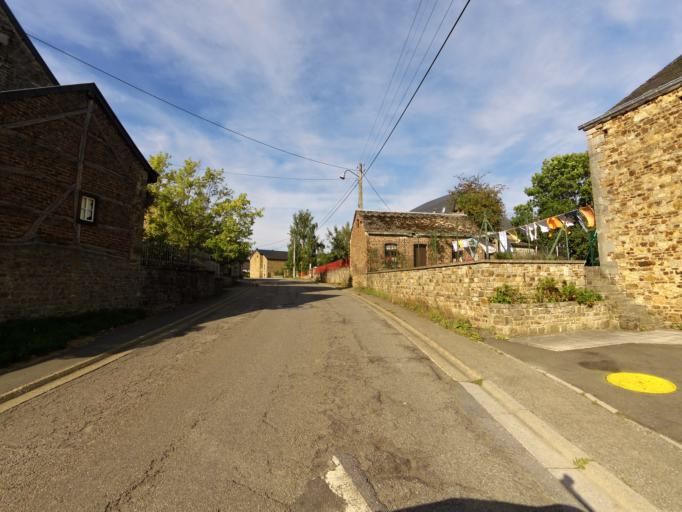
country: BE
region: Wallonia
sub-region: Province du Luxembourg
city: Erezee
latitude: 50.2656
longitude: 5.5596
